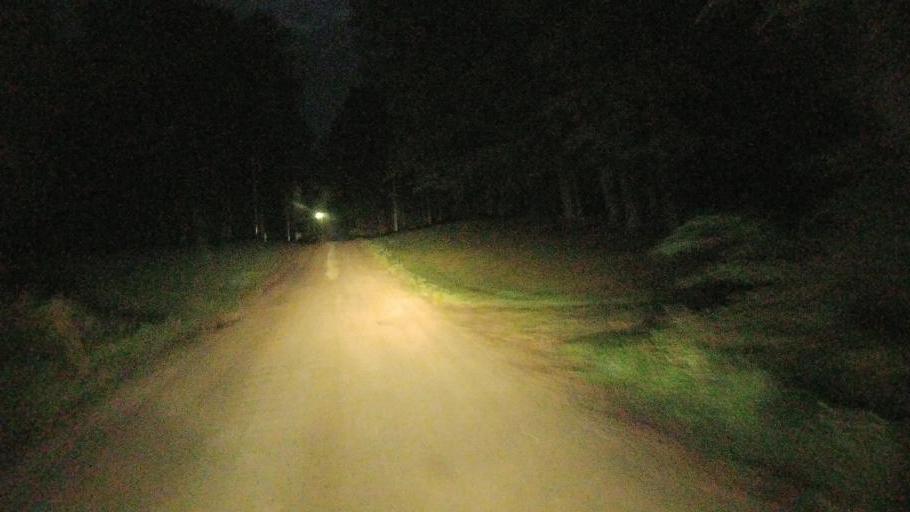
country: US
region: Ohio
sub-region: Richland County
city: Lexington
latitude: 40.5648
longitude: -82.6496
